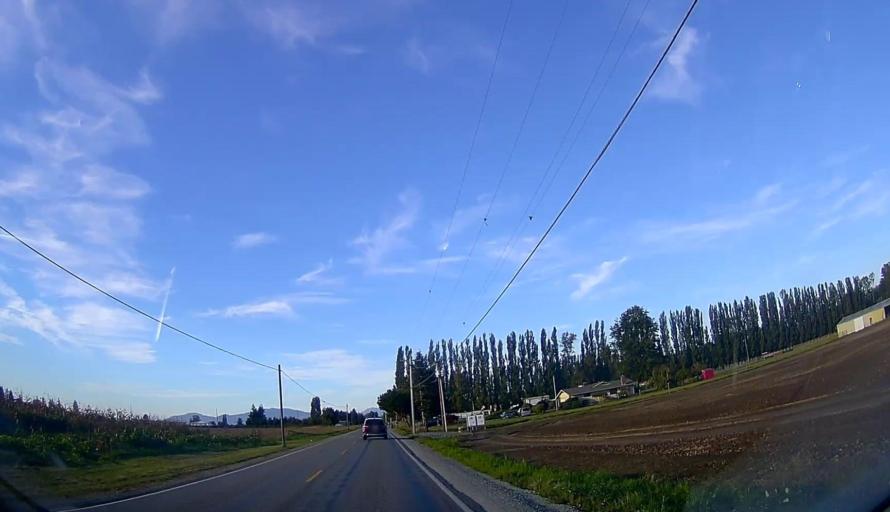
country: US
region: Washington
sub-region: Skagit County
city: Burlington
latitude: 48.4608
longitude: -122.3570
